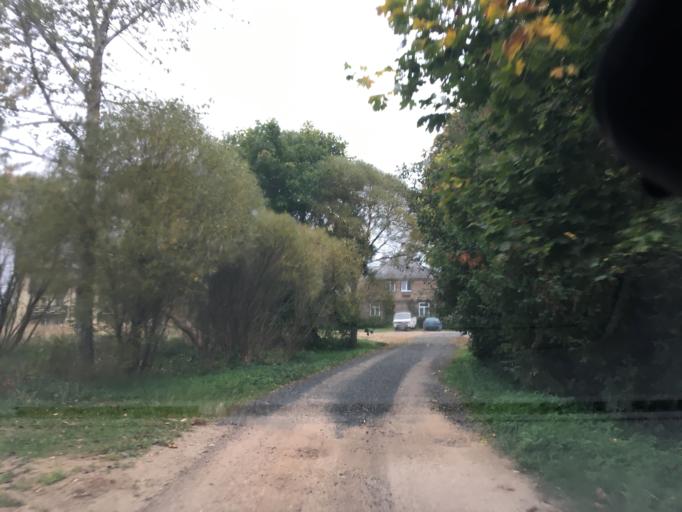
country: LV
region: Kuldigas Rajons
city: Kuldiga
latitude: 56.9846
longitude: 22.0206
